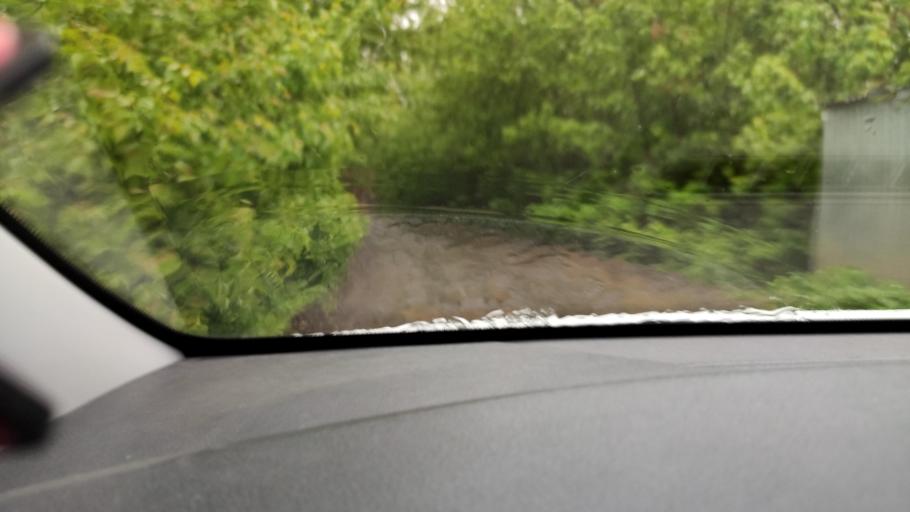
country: RU
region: Tatarstan
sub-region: Gorod Kazan'
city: Kazan
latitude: 55.8108
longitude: 49.2080
